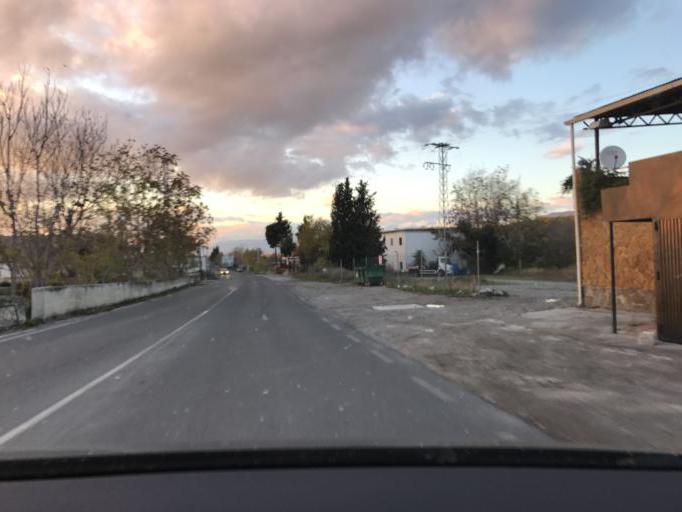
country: ES
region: Andalusia
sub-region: Provincia de Granada
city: Atarfe
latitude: 37.1897
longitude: -3.6776
